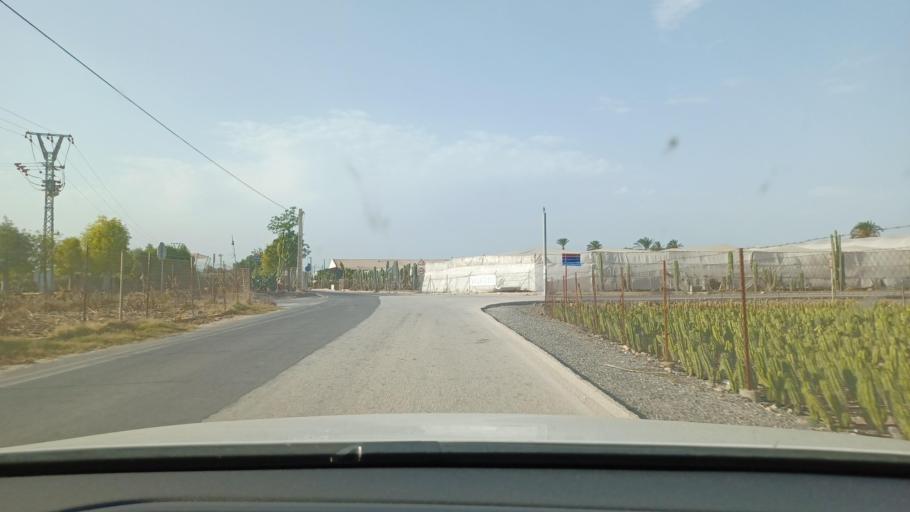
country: ES
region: Valencia
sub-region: Provincia de Alicante
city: Elche
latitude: 38.2416
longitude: -0.6917
